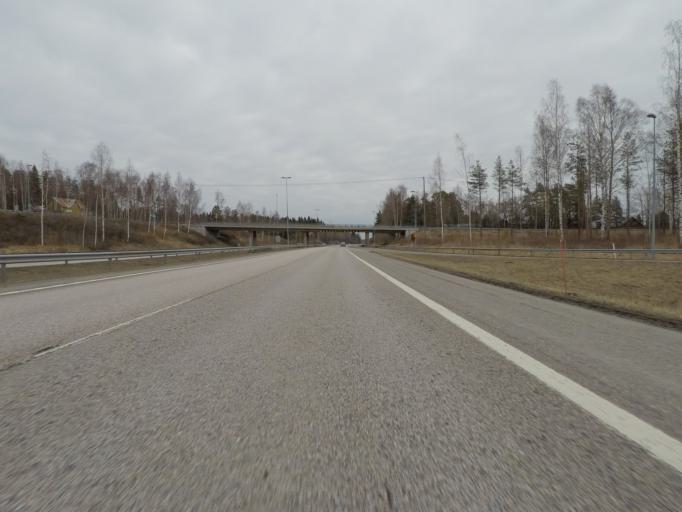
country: FI
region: Uusimaa
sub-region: Helsinki
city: Nickby
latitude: 60.2955
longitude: 25.3579
